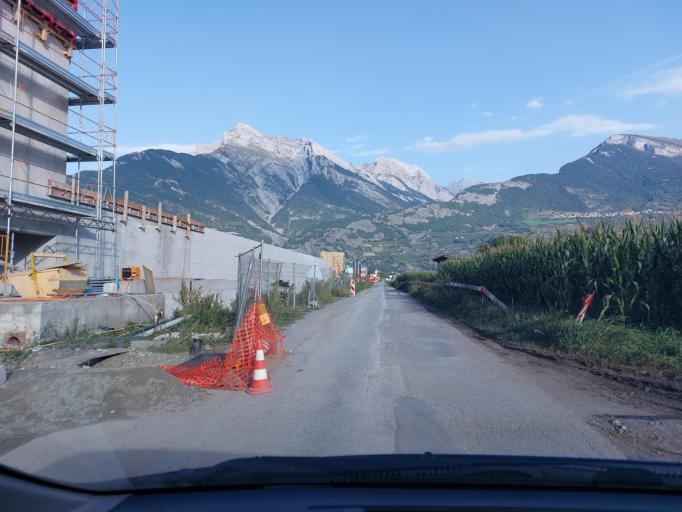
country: CH
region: Valais
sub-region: Conthey District
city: Vetroz
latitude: 46.2026
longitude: 7.2875
